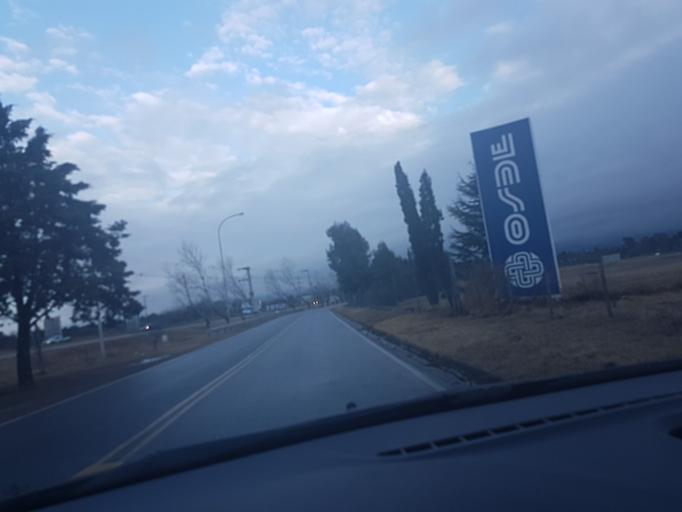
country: AR
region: Cordoba
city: Villa Allende
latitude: -31.3009
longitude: -64.2646
